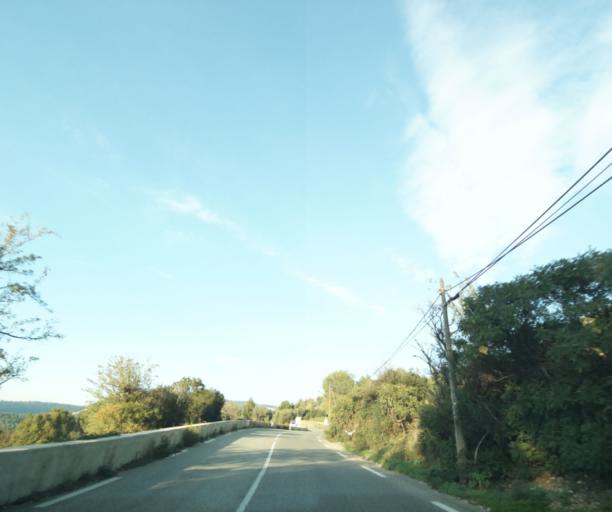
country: FR
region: Provence-Alpes-Cote d'Azur
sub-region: Departement des Bouches-du-Rhone
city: Cassis
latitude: 43.2192
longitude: 5.5671
